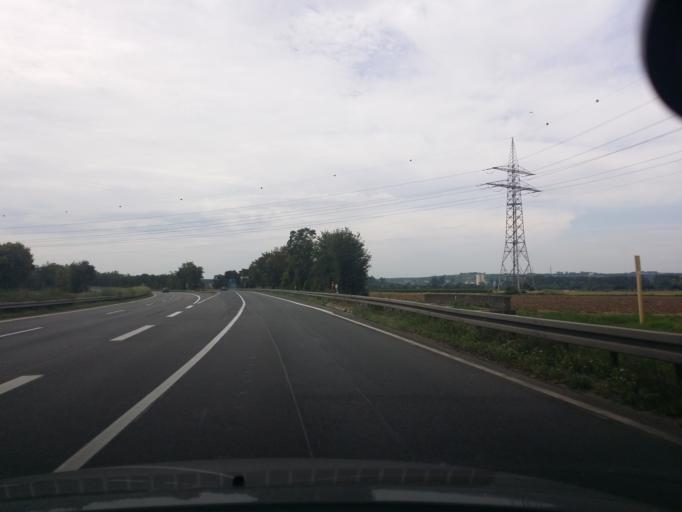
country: DE
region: Hesse
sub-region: Regierungsbezirk Darmstadt
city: Ginsheim-Gustavsburg
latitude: 49.9888
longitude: 8.3389
